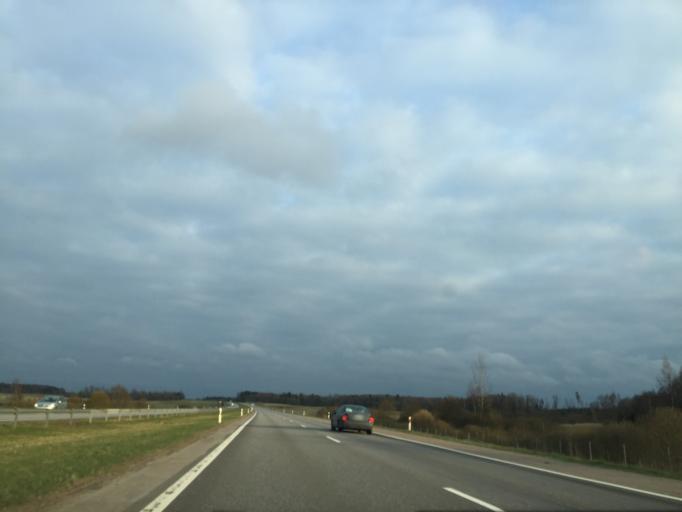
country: LT
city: Rietavas
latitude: 55.6793
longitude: 21.7067
